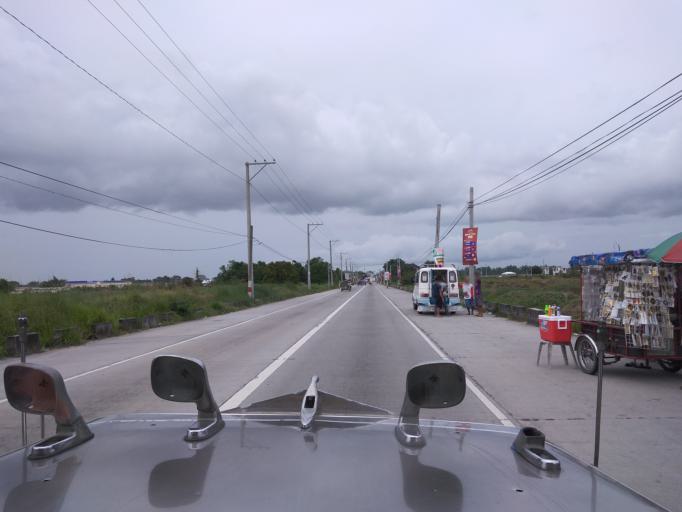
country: PH
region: Central Luzon
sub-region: Province of Pampanga
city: Pandacaqui
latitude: 15.1837
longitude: 120.6302
